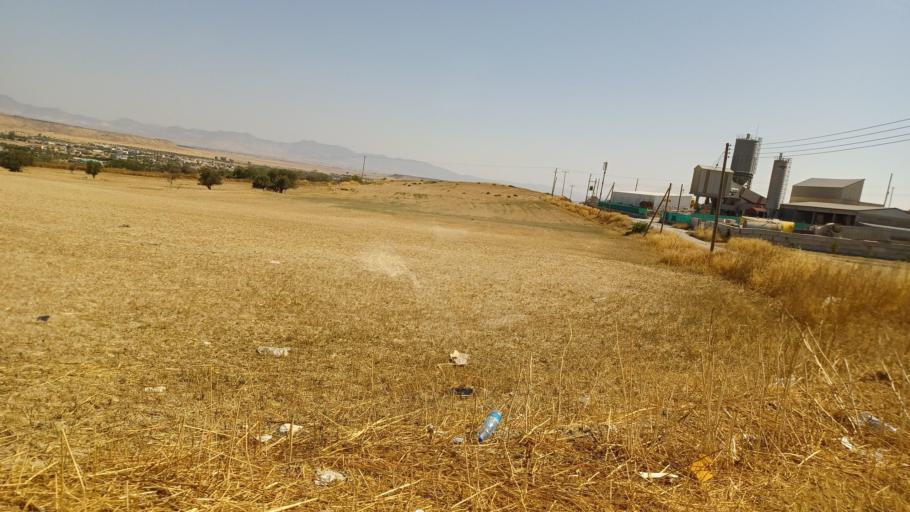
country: CY
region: Larnaka
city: Athienou
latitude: 35.0435
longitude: 33.5343
